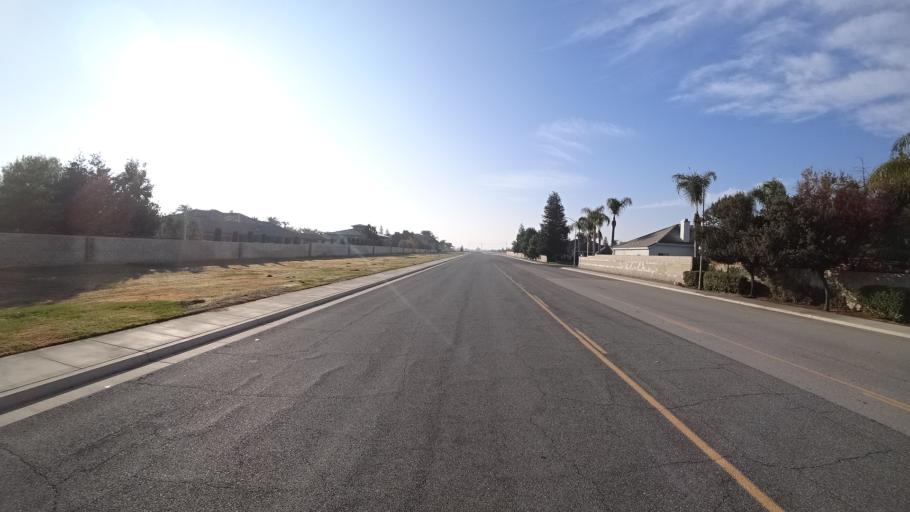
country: US
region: California
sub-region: Kern County
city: Rosedale
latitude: 35.3800
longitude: -119.1722
